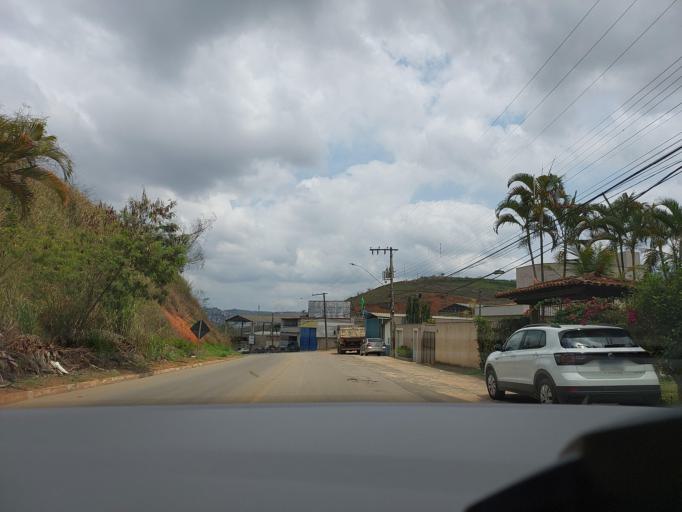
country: BR
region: Minas Gerais
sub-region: Ponte Nova
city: Ponte Nova
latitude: -20.3995
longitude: -42.8837
